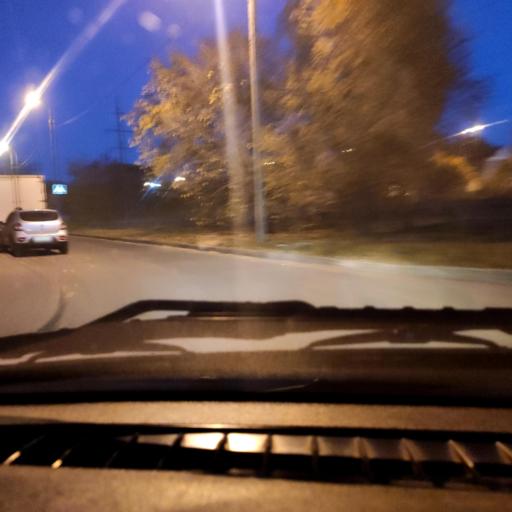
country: RU
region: Samara
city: Zhigulevsk
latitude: 53.4725
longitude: 49.5382
